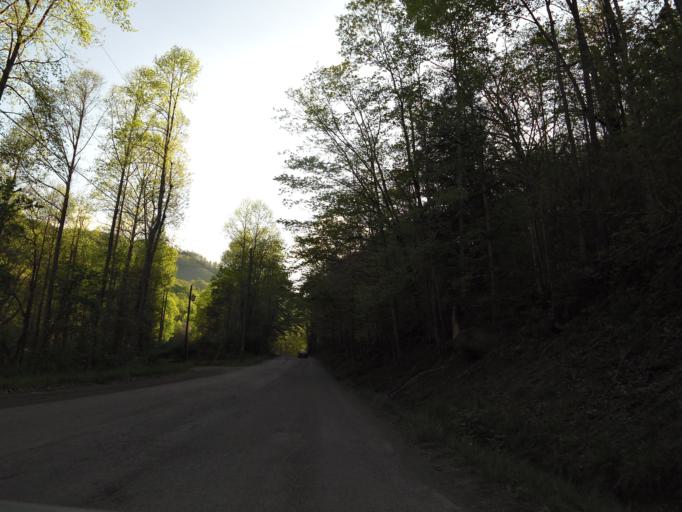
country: US
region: Kentucky
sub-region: Bell County
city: Middlesboro
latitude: 36.6097
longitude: -83.8102
